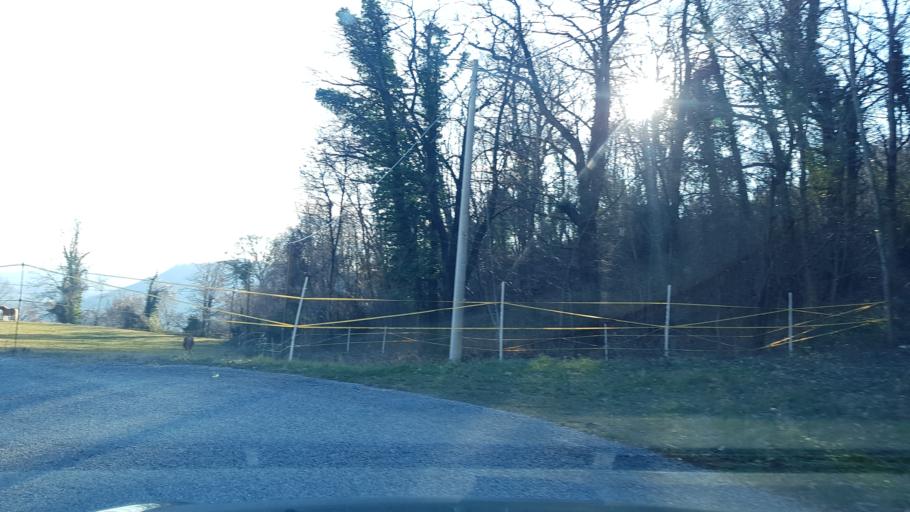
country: IT
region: Friuli Venezia Giulia
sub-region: Provincia di Udine
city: Forgaria nel Friuli
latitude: 46.2297
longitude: 12.9966
